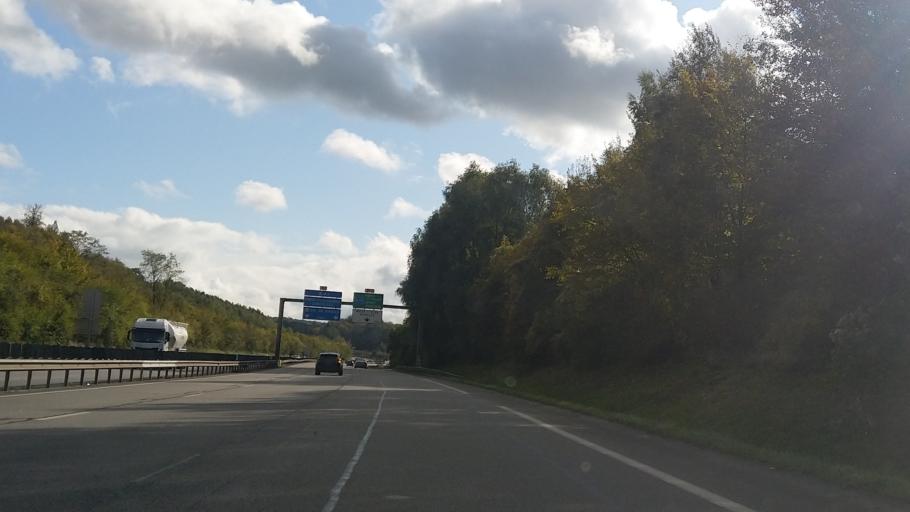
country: FR
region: Ile-de-France
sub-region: Departement du Val-d'Oise
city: Mours
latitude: 49.1152
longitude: 2.2532
